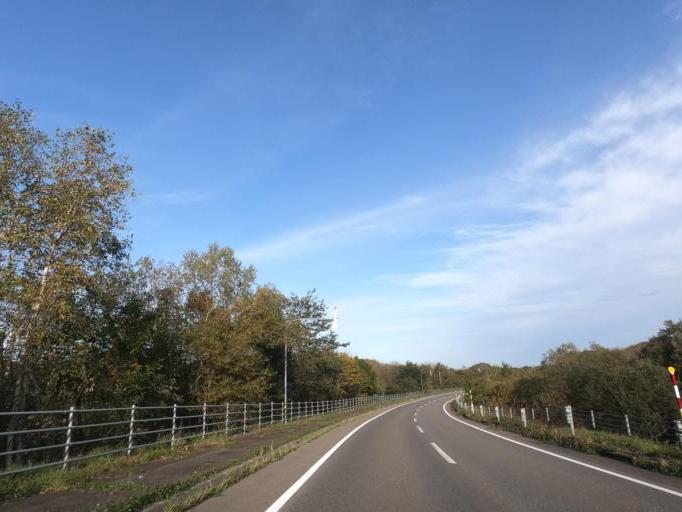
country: JP
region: Hokkaido
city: Obihiro
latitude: 42.5006
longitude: 143.4037
